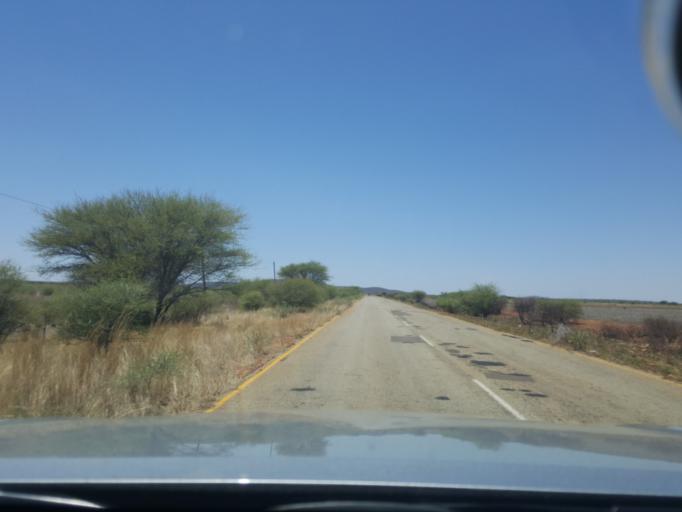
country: BW
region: South East
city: Ramotswa
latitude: -25.0675
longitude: 25.9461
